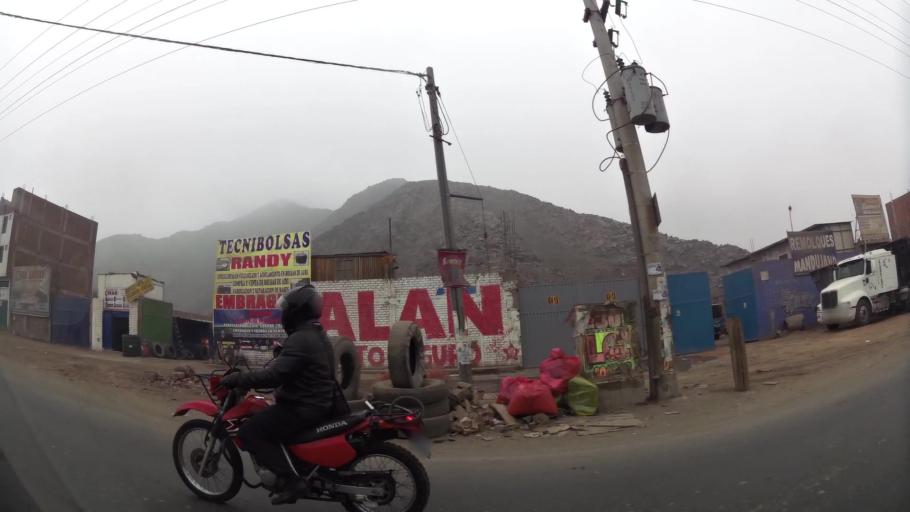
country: PE
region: Lima
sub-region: Lima
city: Santa Maria
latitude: -12.0094
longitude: -76.8664
